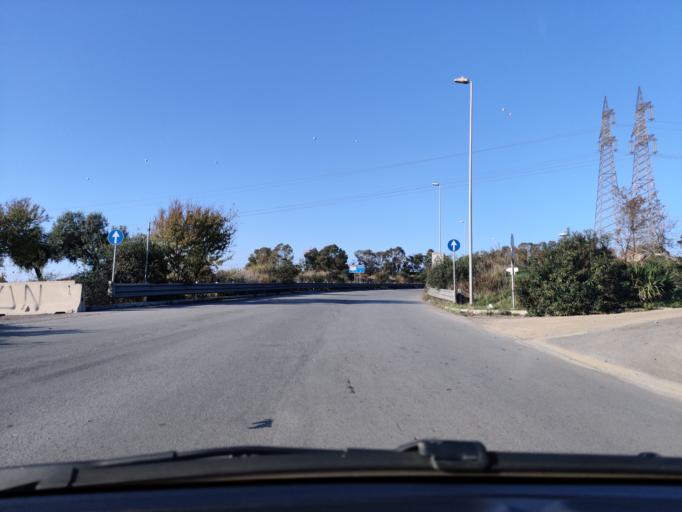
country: IT
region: Latium
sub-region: Citta metropolitana di Roma Capitale
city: Aurelia
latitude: 42.1326
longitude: 11.7759
